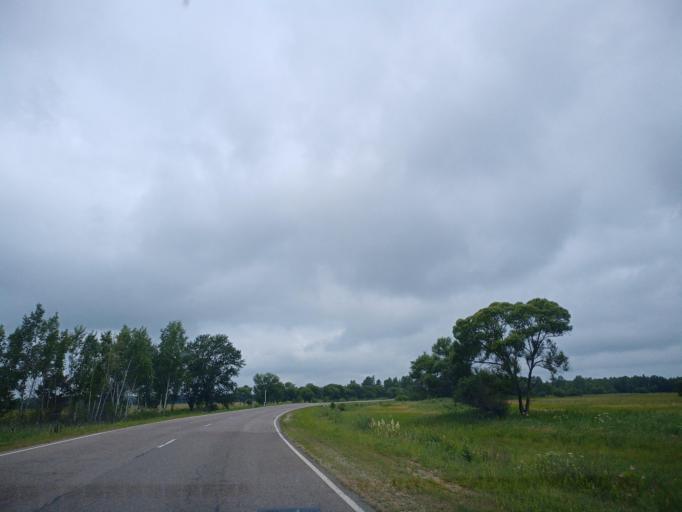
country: RU
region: Primorskiy
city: Novopokrovka
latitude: 45.9641
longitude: 134.2535
